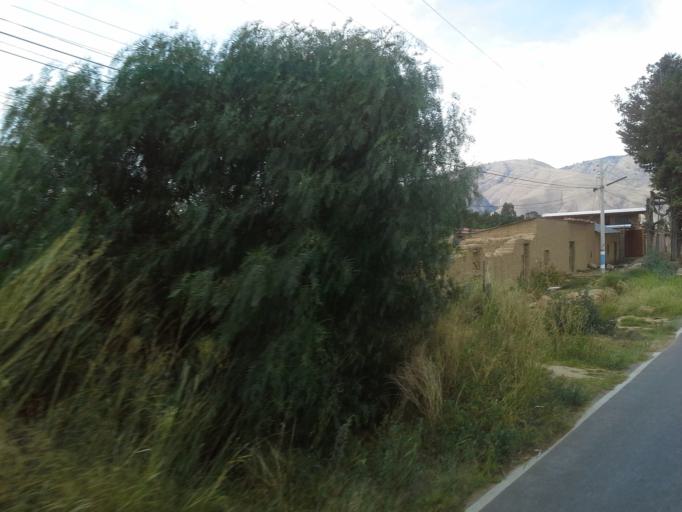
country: BO
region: Cochabamba
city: Tarata
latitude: -17.5670
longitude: -66.0116
